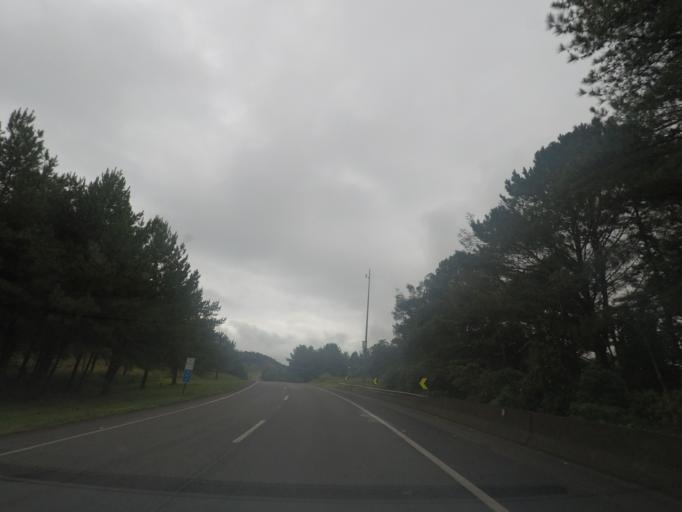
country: BR
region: Parana
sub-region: Antonina
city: Antonina
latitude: -25.0830
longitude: -48.6425
